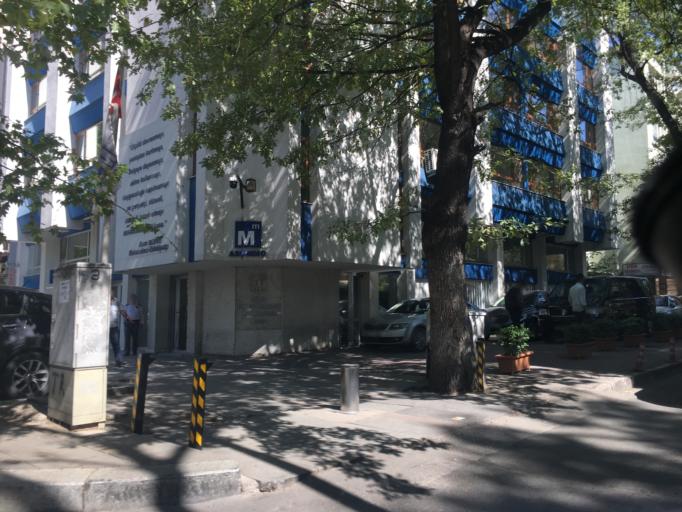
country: TR
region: Ankara
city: Ankara
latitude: 39.9208
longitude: 32.8489
